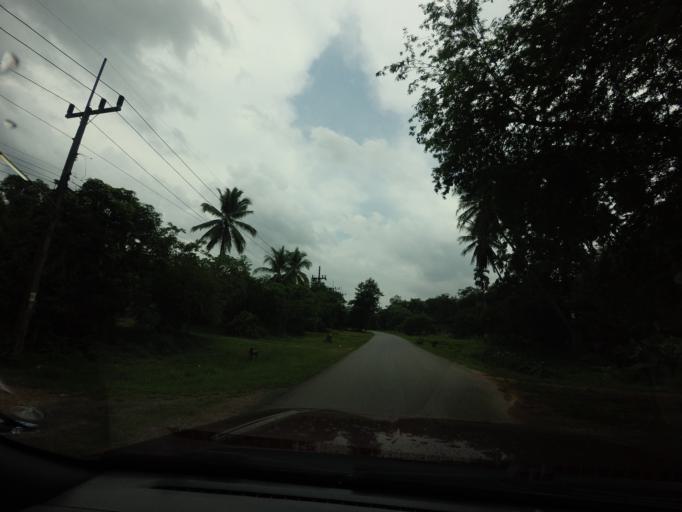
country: TH
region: Yala
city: Ban Nang Sata
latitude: 6.2066
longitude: 101.2352
